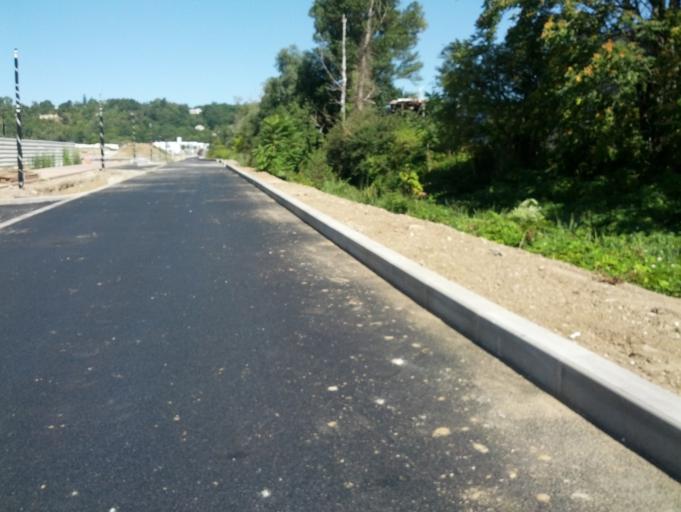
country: FR
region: Aquitaine
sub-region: Departement de la Gironde
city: Floirac
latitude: 44.8234
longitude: -0.5307
